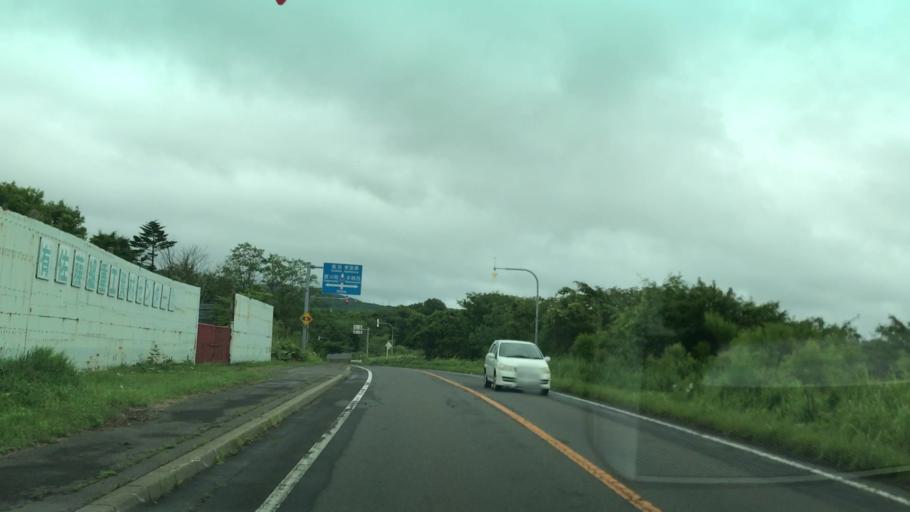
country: JP
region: Hokkaido
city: Muroran
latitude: 42.3842
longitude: 140.9817
